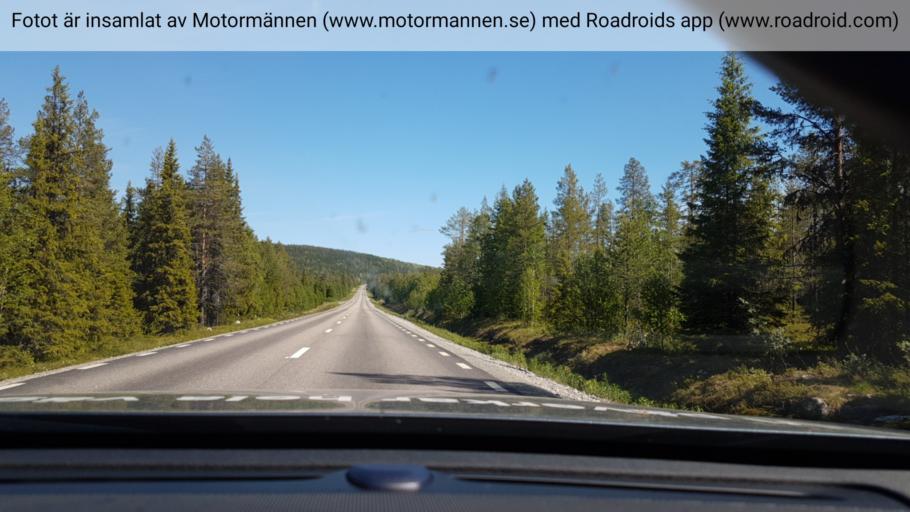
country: SE
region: Vaesterbotten
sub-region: Asele Kommun
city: Insjon
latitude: 64.7223
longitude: 17.6300
